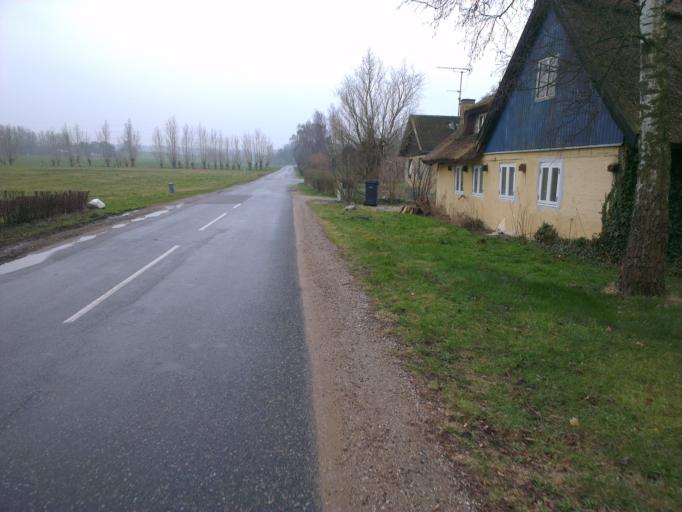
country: DK
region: Capital Region
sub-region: Frederikssund Kommune
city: Jaegerspris
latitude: 55.8119
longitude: 11.9517
